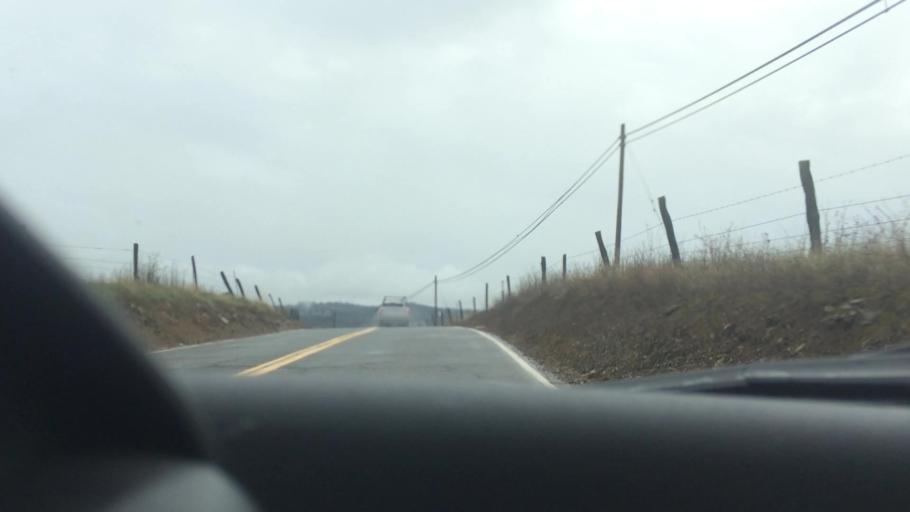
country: US
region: California
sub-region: El Dorado County
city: Cameron Park
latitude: 38.6068
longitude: -121.0345
